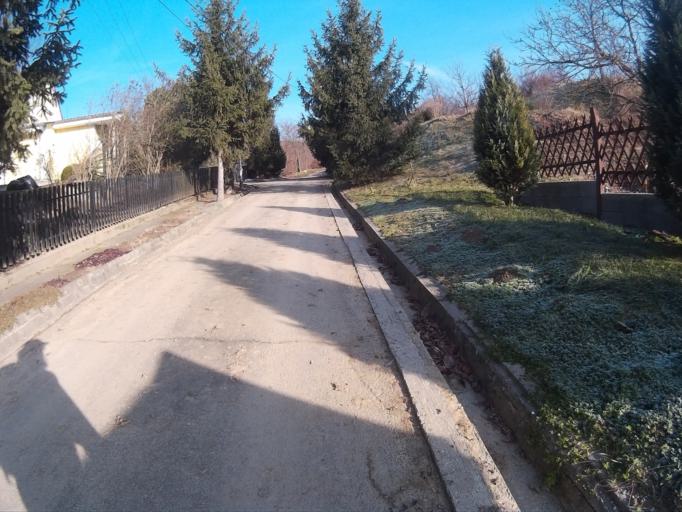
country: HU
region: Nograd
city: Bercel
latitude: 47.9296
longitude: 19.4113
